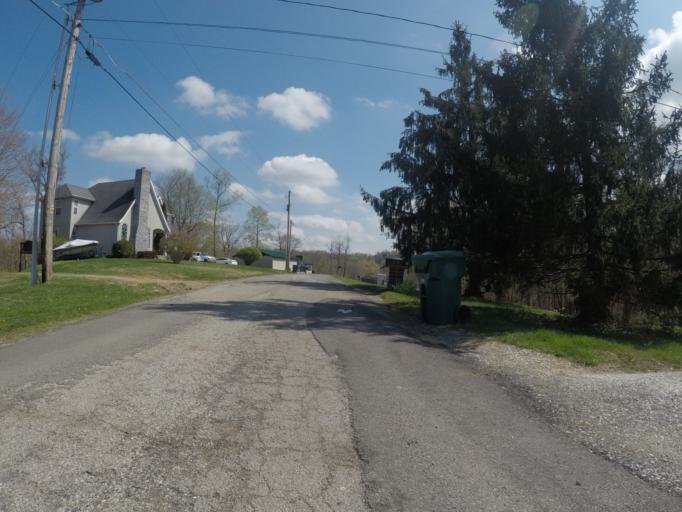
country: US
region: Ohio
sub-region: Lawrence County
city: Burlington
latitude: 38.3913
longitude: -82.5380
